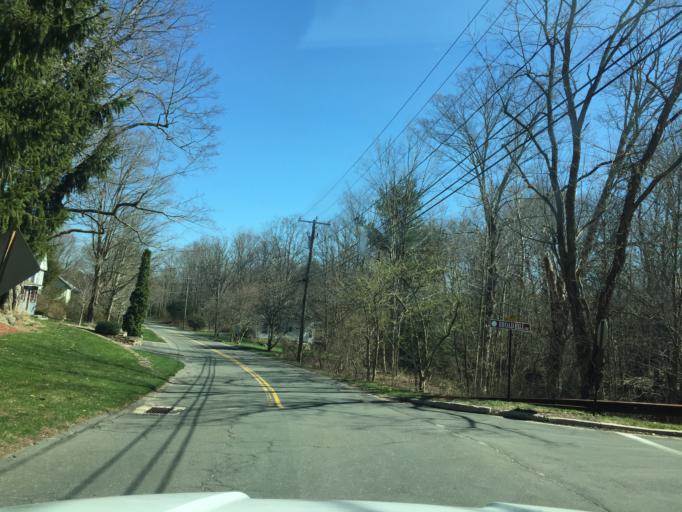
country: US
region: Connecticut
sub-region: Hartford County
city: North Granby
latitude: 41.9554
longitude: -72.8433
